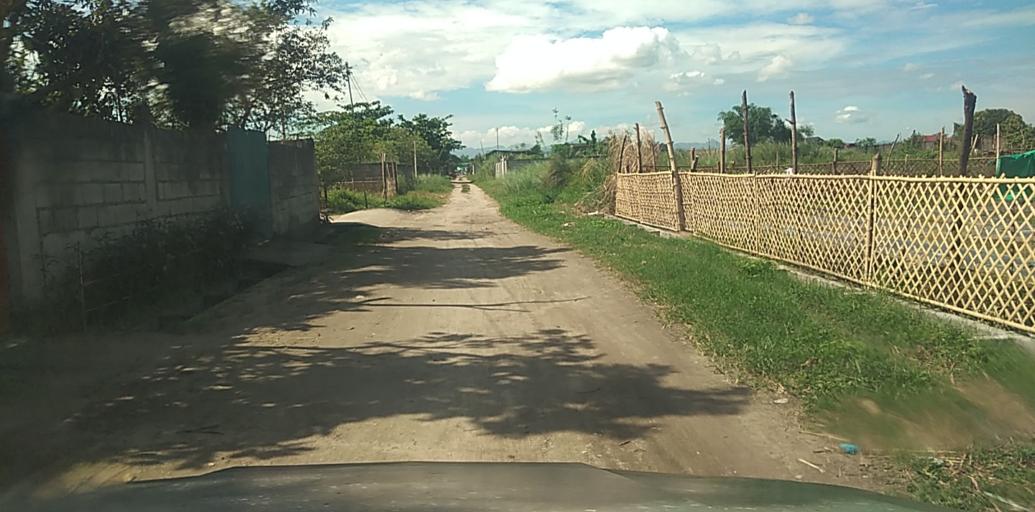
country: PH
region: Central Luzon
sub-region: Province of Pampanga
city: Buensuseso
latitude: 15.1943
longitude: 120.6703
